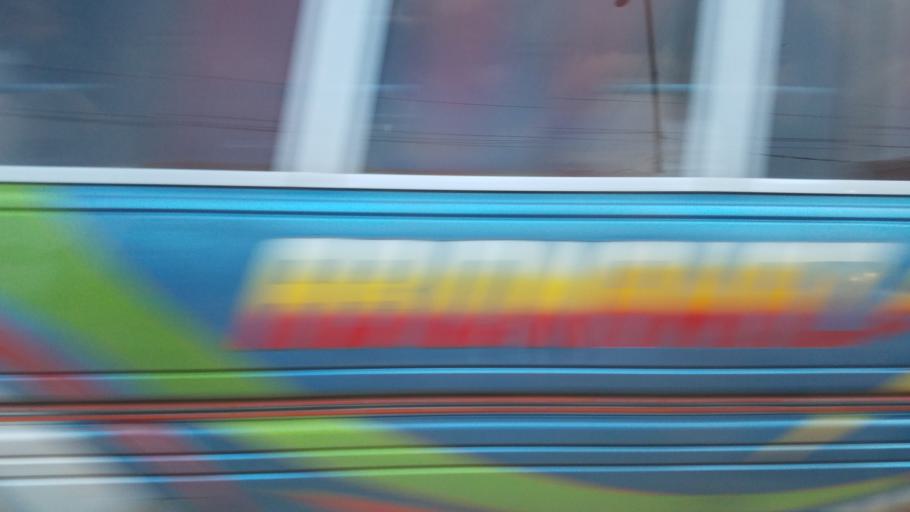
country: PK
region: Sindh
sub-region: Karachi District
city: Karachi
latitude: 24.9314
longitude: 67.0864
